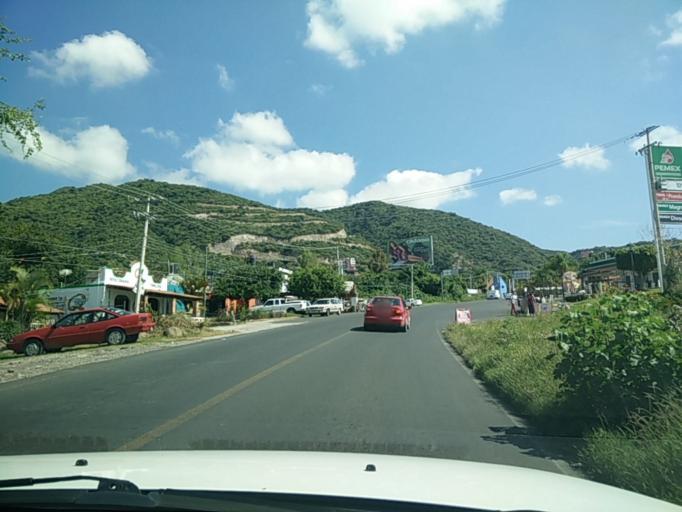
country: MX
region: Jalisco
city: Ajijic
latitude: 20.3007
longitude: -103.2434
